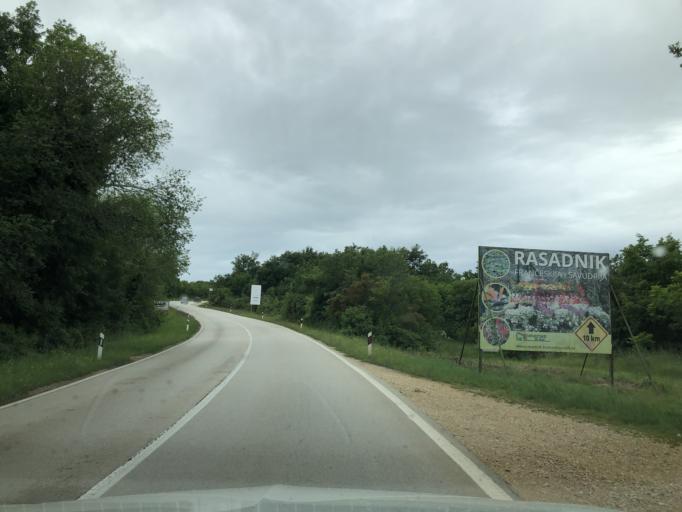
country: SI
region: Piran-Pirano
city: Seca
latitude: 45.4574
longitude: 13.6113
